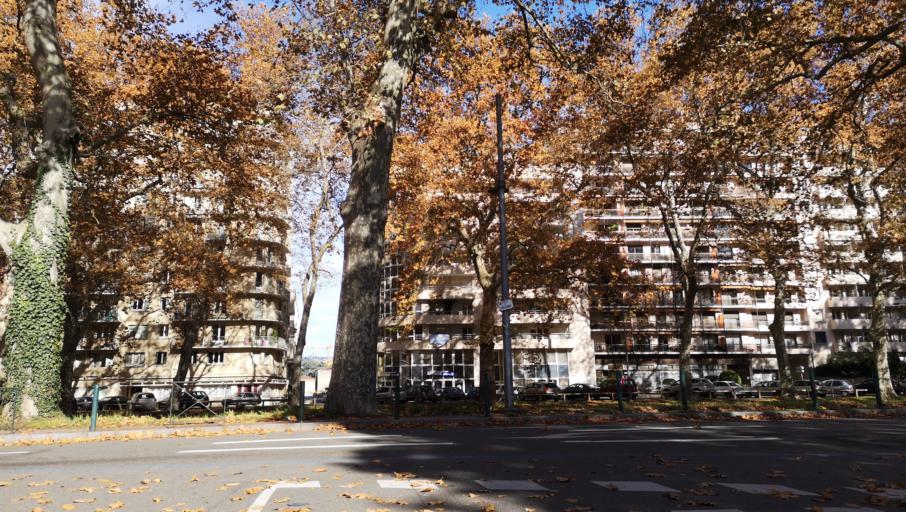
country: FR
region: Midi-Pyrenees
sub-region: Departement de la Haute-Garonne
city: Toulouse
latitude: 43.6053
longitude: 1.4325
